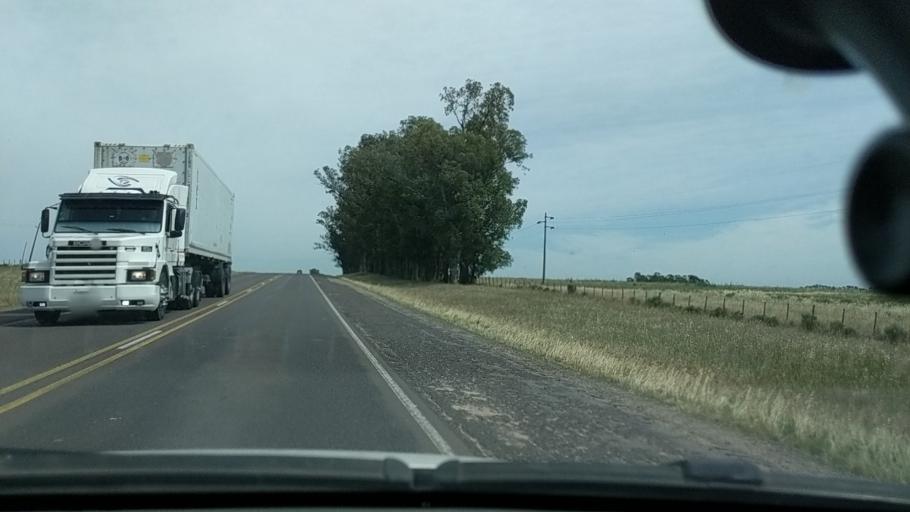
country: UY
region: Durazno
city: Durazno
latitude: -33.4847
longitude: -56.4398
